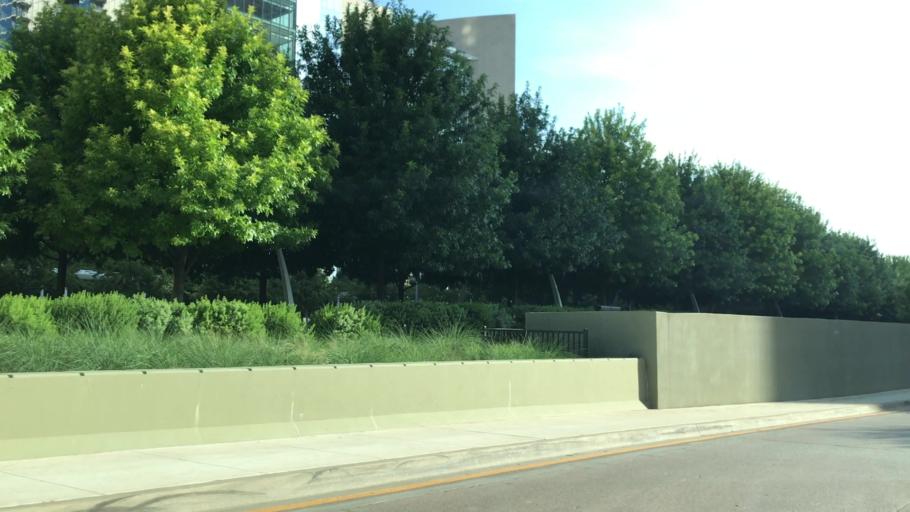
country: US
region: Texas
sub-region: Dallas County
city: Dallas
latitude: 32.7895
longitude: -96.8009
